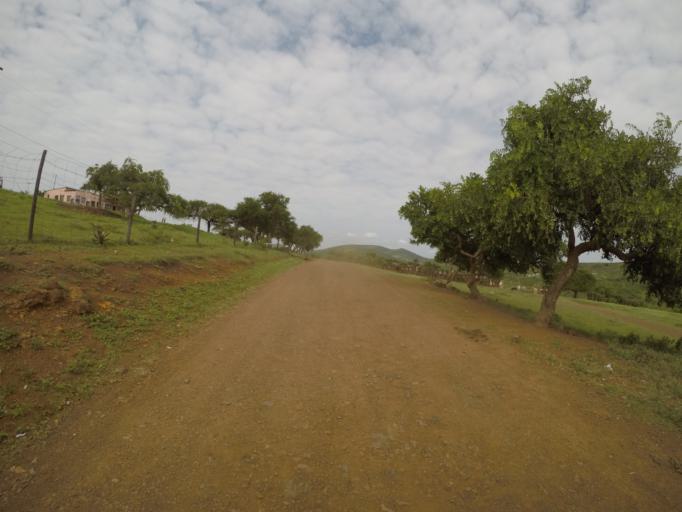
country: ZA
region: KwaZulu-Natal
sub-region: uThungulu District Municipality
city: Empangeni
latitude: -28.6231
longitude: 31.9009
